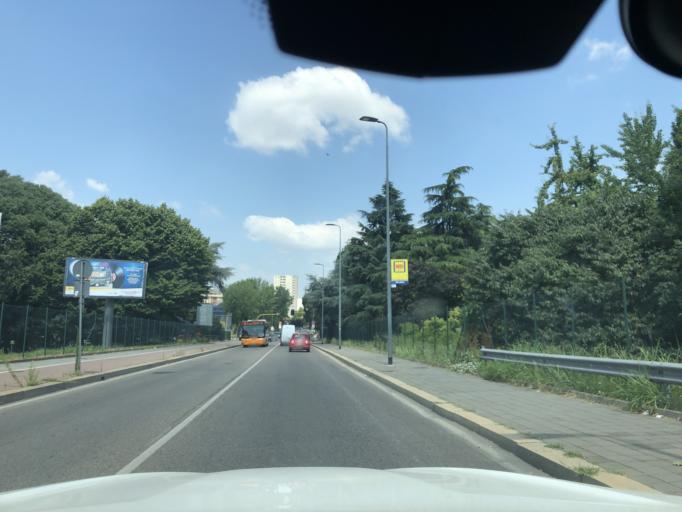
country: IT
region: Lombardy
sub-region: Citta metropolitana di Milano
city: Sesto San Giovanni
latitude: 45.5075
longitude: 9.2103
